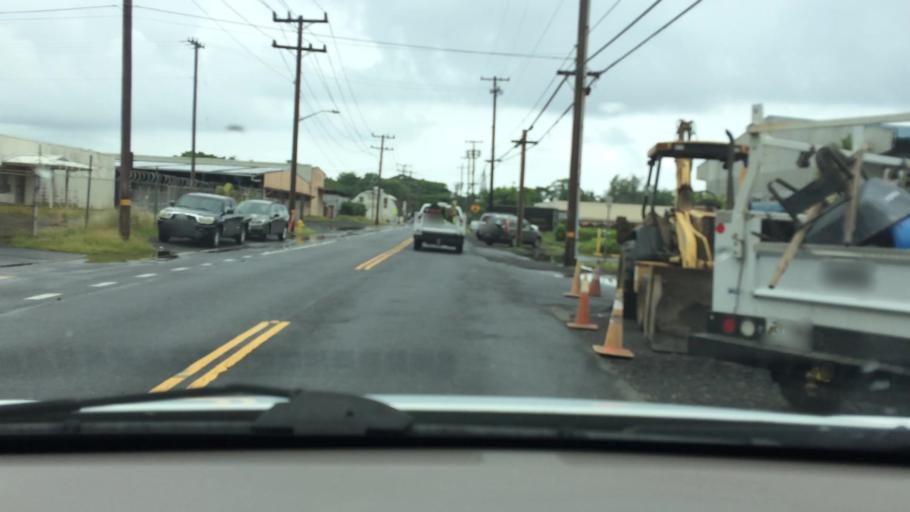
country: US
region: Hawaii
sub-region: Hawaii County
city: Hilo
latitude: 19.7196
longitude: -155.0657
